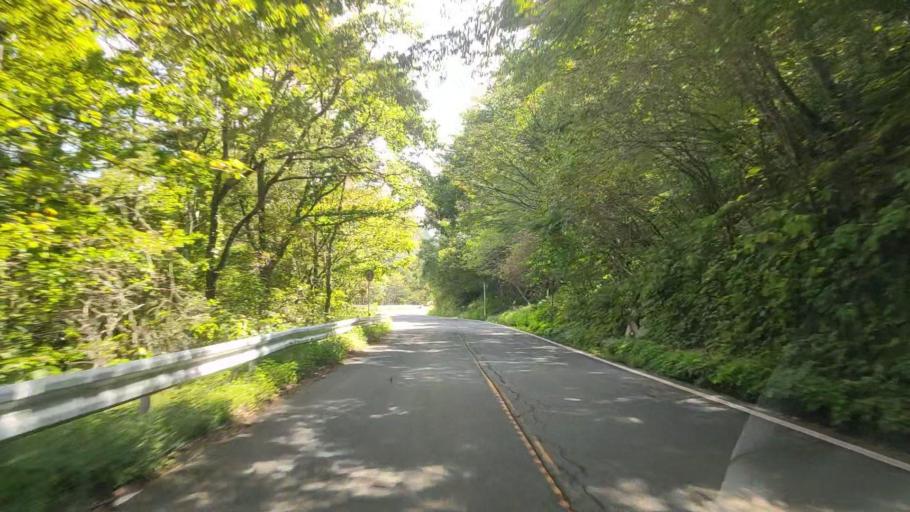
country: JP
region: Gunma
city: Shibukawa
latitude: 36.4866
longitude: 138.8972
